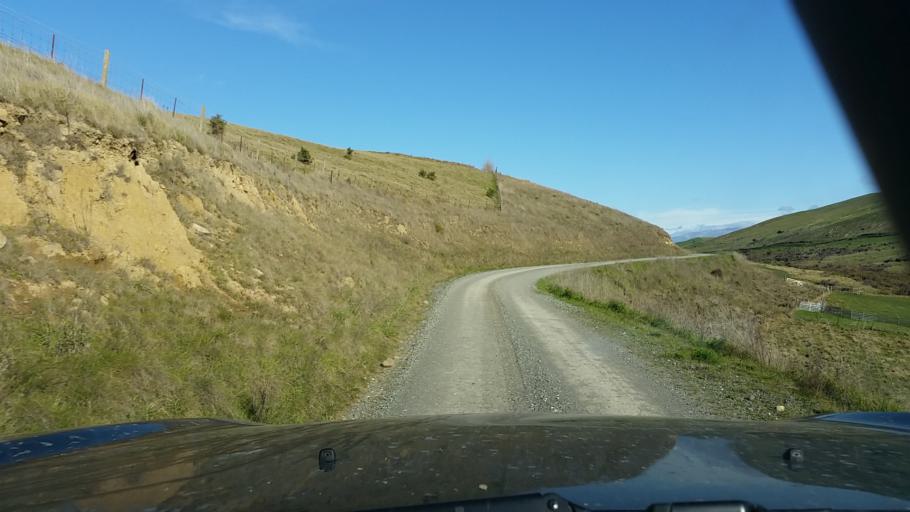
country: NZ
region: Marlborough
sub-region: Marlborough District
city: Blenheim
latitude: -41.6674
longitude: 174.1403
